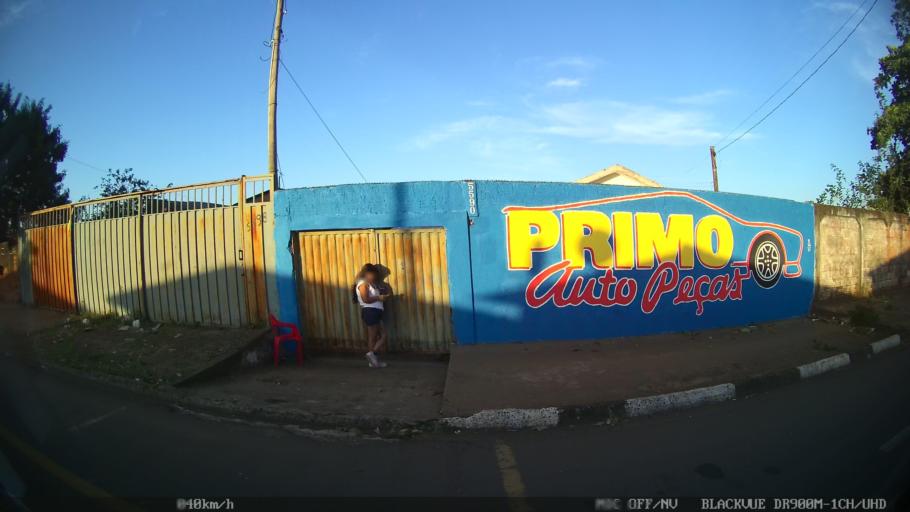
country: BR
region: Sao Paulo
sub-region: Franca
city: Franca
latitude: -20.5025
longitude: -47.3978
